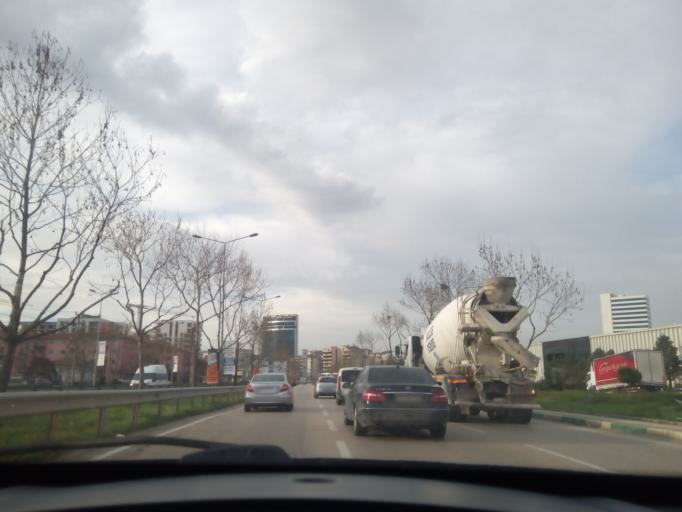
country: TR
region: Bursa
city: Cali
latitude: 40.2226
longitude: 28.9557
